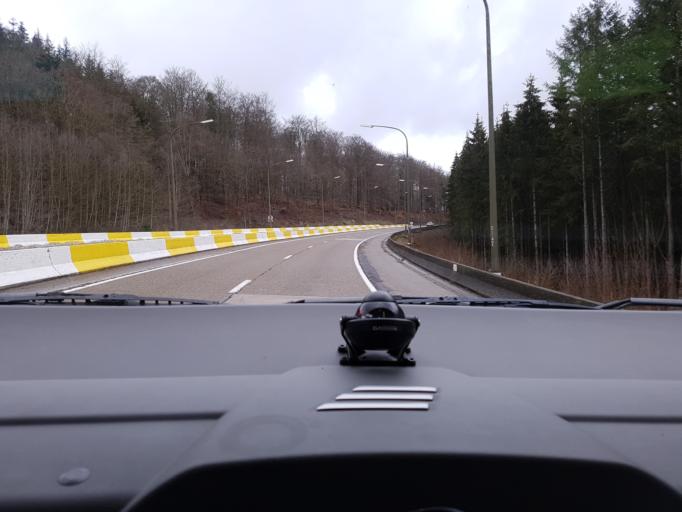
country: BE
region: Wallonia
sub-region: Province du Luxembourg
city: Tenneville
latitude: 50.0936
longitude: 5.4871
